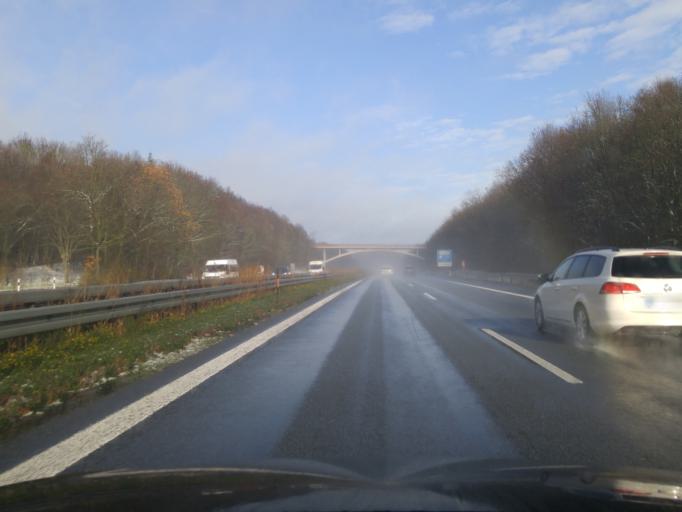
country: DE
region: Bavaria
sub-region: Regierungsbezirk Unterfranken
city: Rimpar
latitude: 49.8814
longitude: 9.9954
